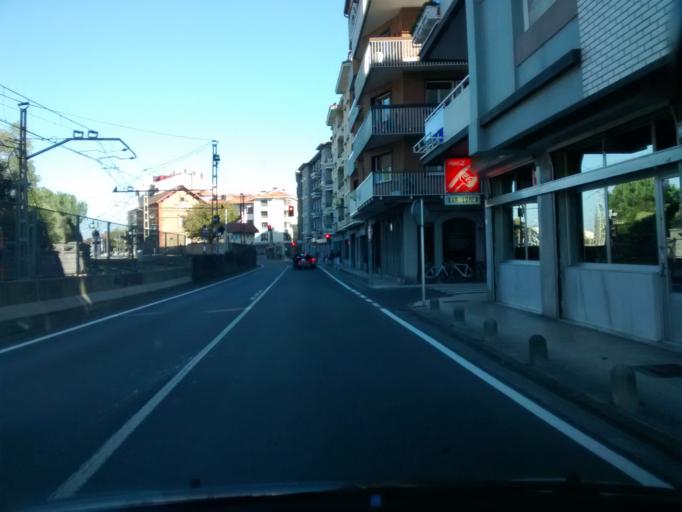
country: ES
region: Basque Country
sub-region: Provincia de Guipuzcoa
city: Deba
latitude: 43.2926
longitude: -2.3559
